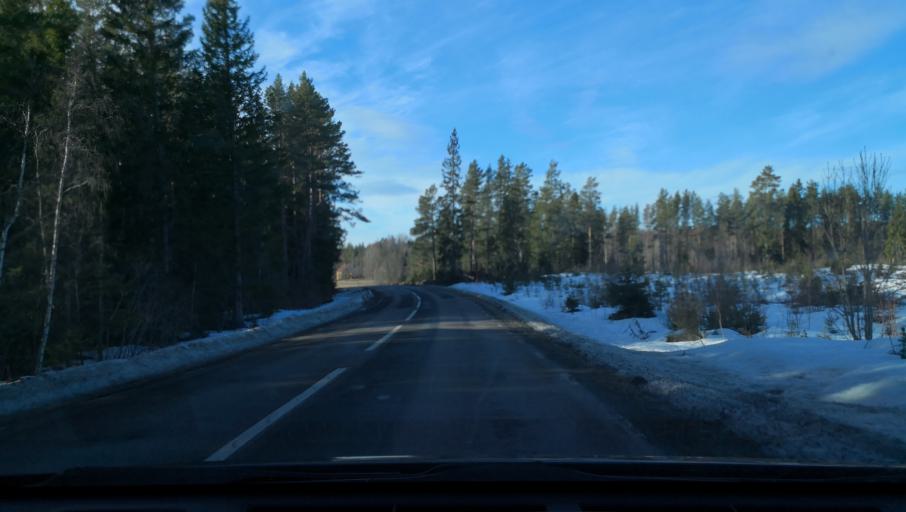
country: SE
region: Uppsala
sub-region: Osthammars Kommun
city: Osterbybruk
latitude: 60.2901
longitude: 18.0305
